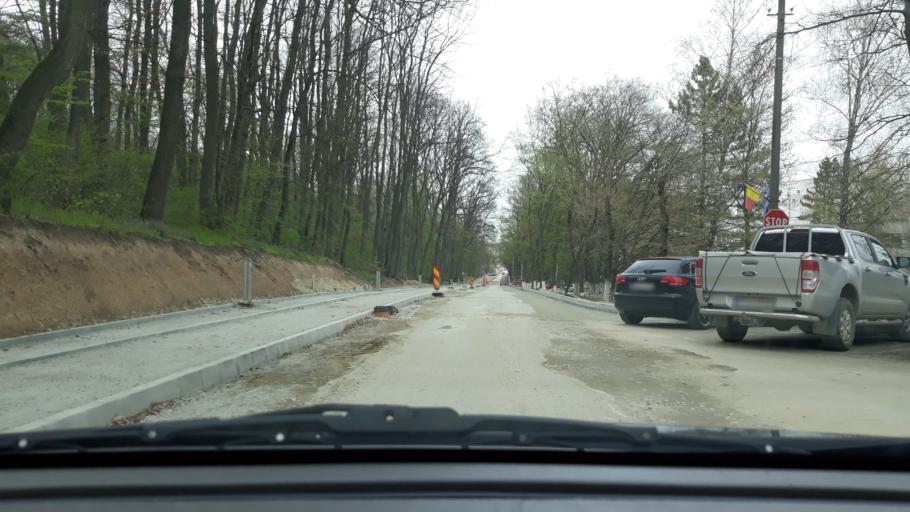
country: RO
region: Bihor
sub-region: Comuna Sanmartin
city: Sanmartin
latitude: 46.9919
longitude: 21.9765
